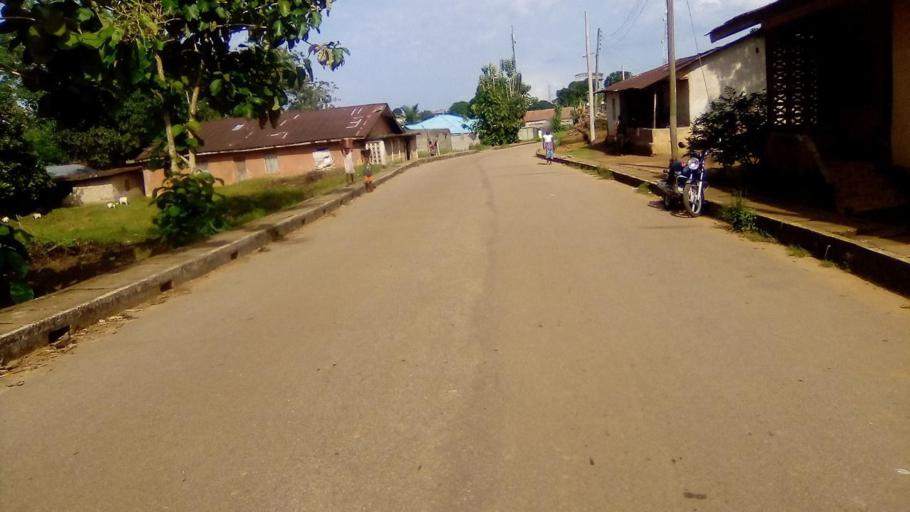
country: SL
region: Southern Province
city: Pujehun
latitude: 7.3580
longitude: -11.7174
